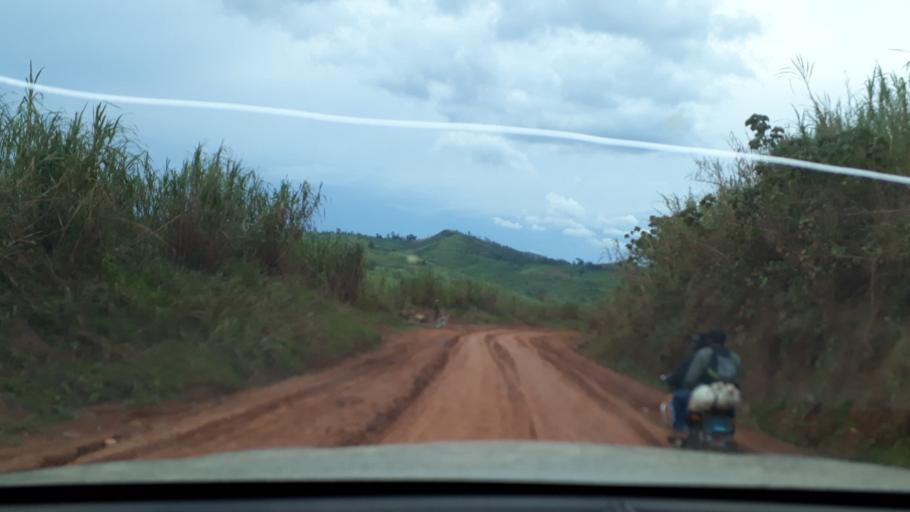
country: CD
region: Eastern Province
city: Bunia
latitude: 1.7646
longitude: 30.3843
